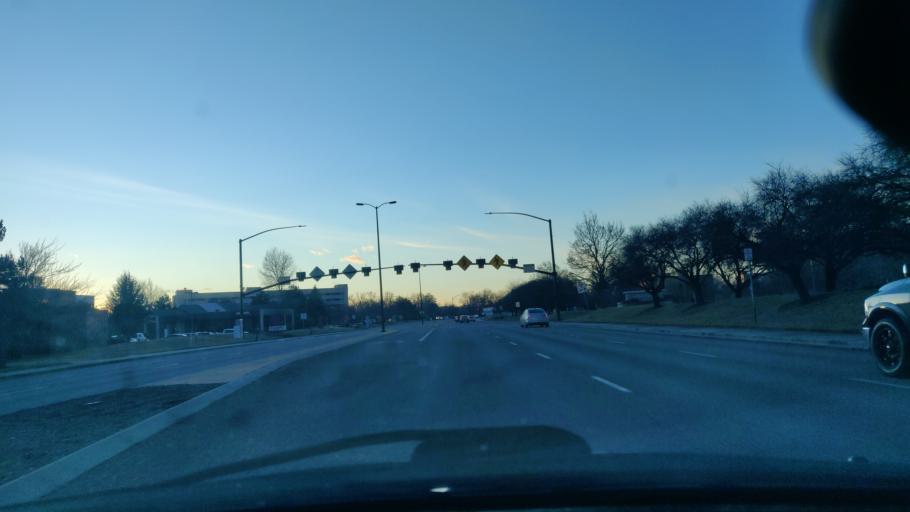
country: US
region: Idaho
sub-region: Ada County
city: Boise
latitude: 43.5988
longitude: -116.1829
